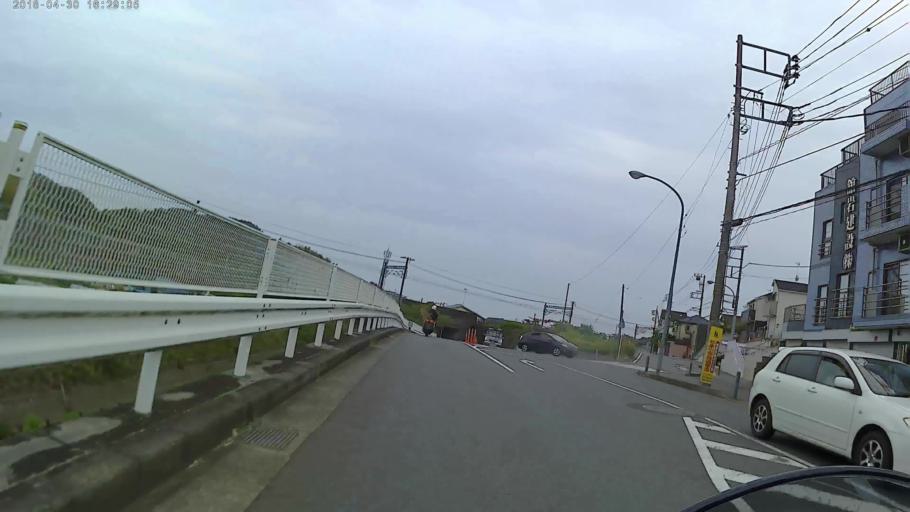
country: JP
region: Kanagawa
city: Zama
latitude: 35.4602
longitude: 139.4052
